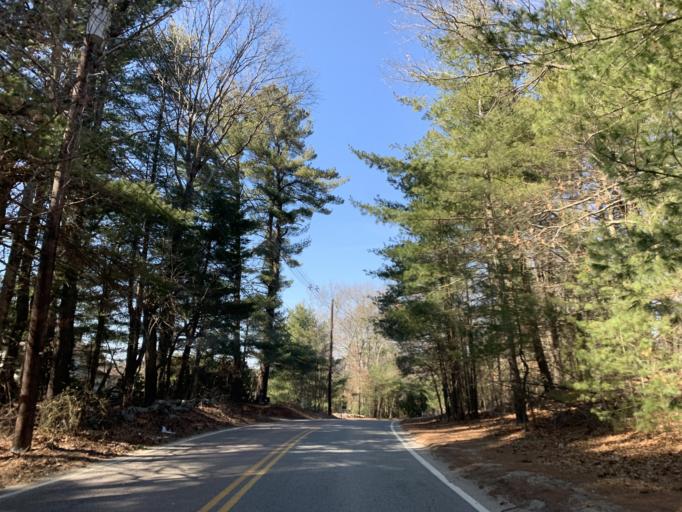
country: US
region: Massachusetts
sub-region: Norfolk County
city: Sharon
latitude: 42.1460
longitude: -71.1771
